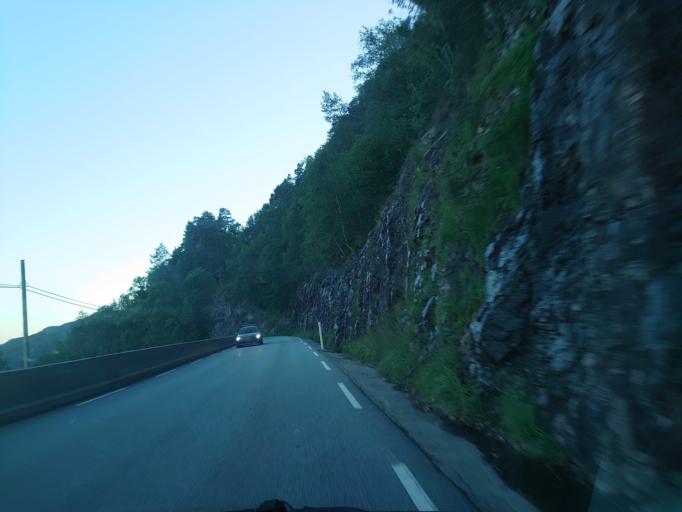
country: NO
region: Hordaland
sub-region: Osteroy
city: Lonevag
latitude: 60.7079
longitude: 5.6099
